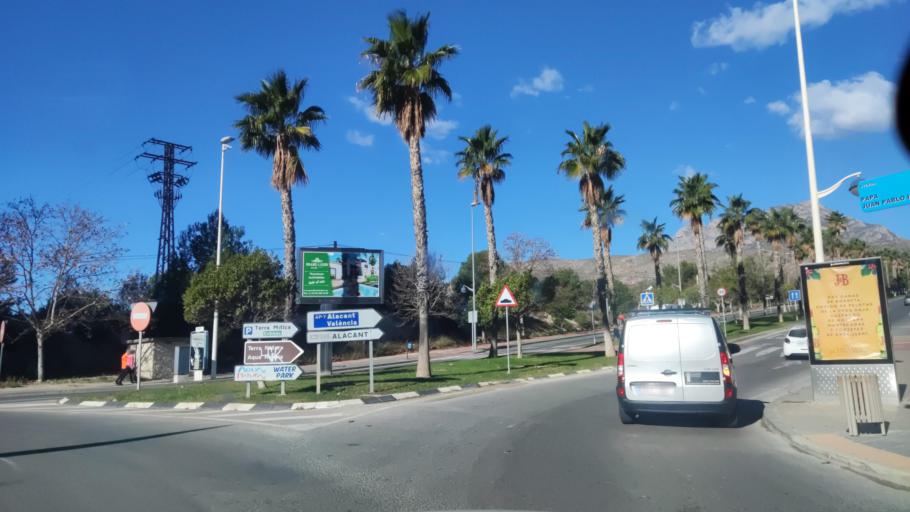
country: ES
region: Valencia
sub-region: Provincia de Alicante
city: Benidorm
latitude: 38.5379
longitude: -0.1583
